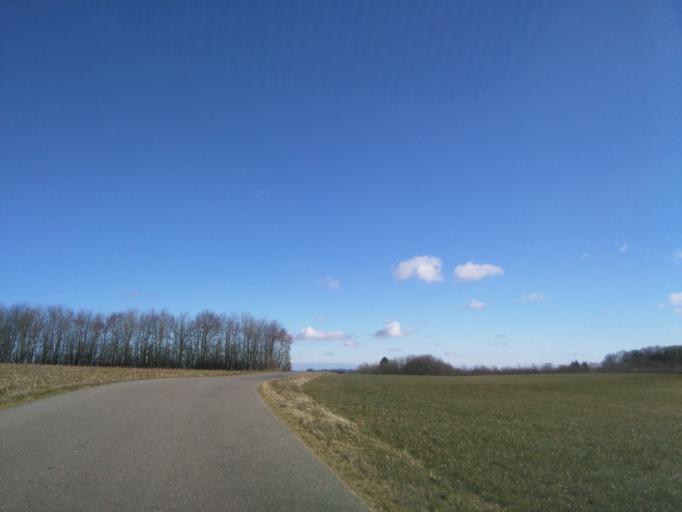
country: DK
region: Central Jutland
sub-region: Skanderborg Kommune
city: Ry
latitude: 56.1341
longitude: 9.7552
